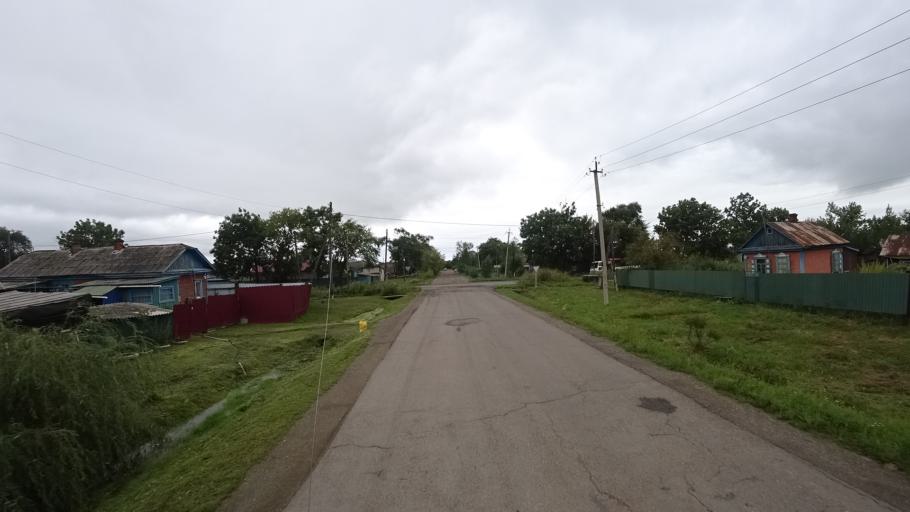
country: RU
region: Primorskiy
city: Chernigovka
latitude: 44.3476
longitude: 132.5641
